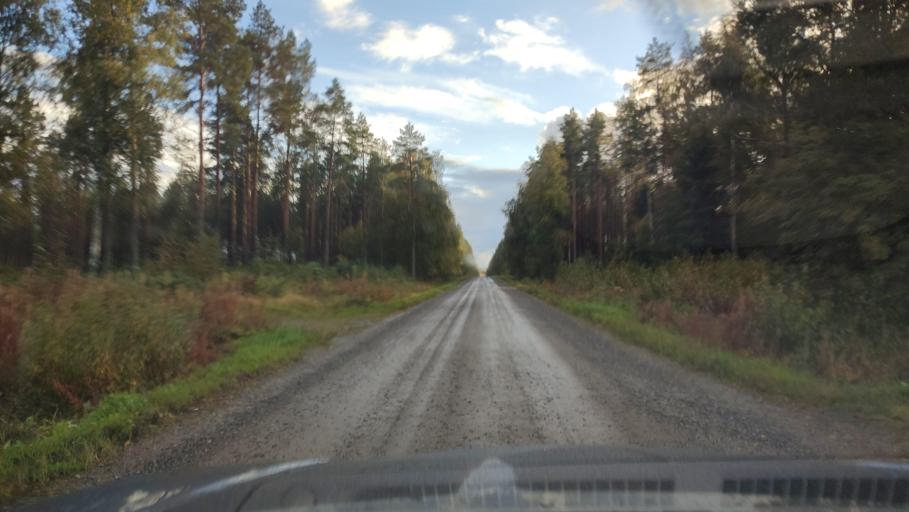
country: FI
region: Southern Ostrobothnia
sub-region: Suupohja
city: Karijoki
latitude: 62.3206
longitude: 21.5656
